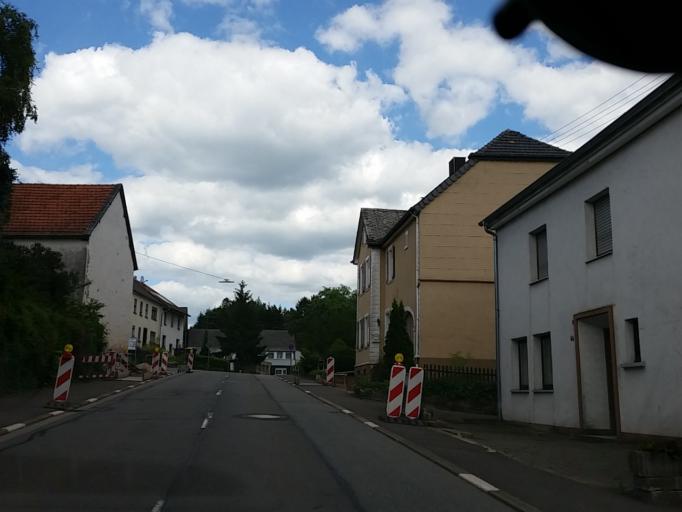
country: DE
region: Saarland
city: Wadern
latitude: 49.5262
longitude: 6.9209
